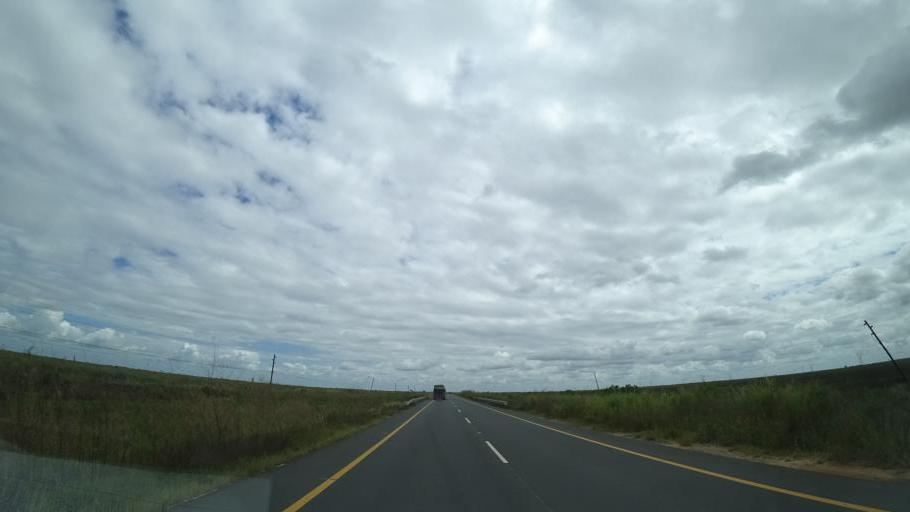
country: MZ
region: Sofala
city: Dondo
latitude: -19.4868
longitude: 34.5800
